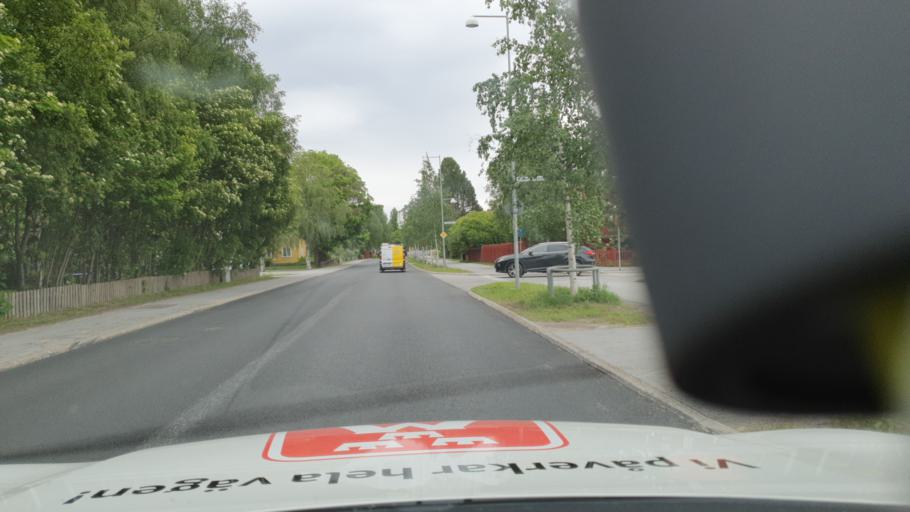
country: SE
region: Vaesterbotten
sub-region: Umea Kommun
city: Umea
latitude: 63.8328
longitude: 20.2189
